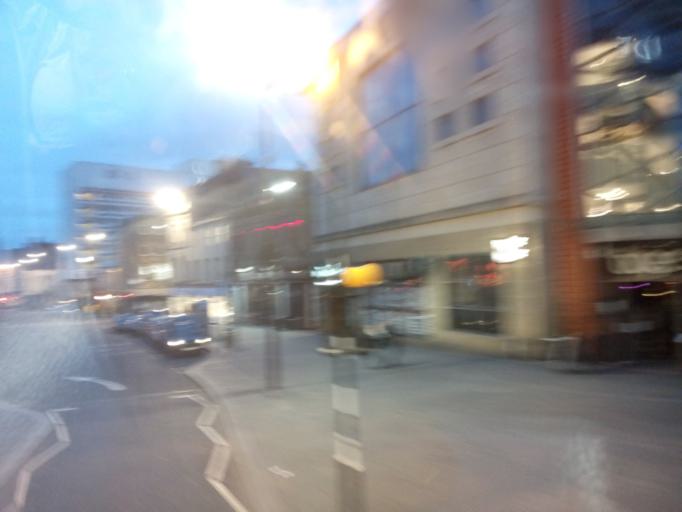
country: GB
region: England
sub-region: Newcastle upon Tyne
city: Newcastle upon Tyne
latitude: 54.9727
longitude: -1.6173
